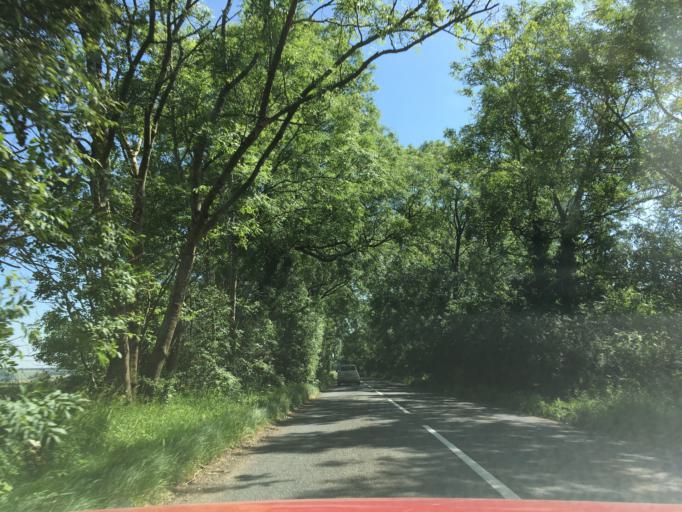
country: GB
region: England
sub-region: Gloucestershire
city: Westfield
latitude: 51.8978
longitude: -1.8814
